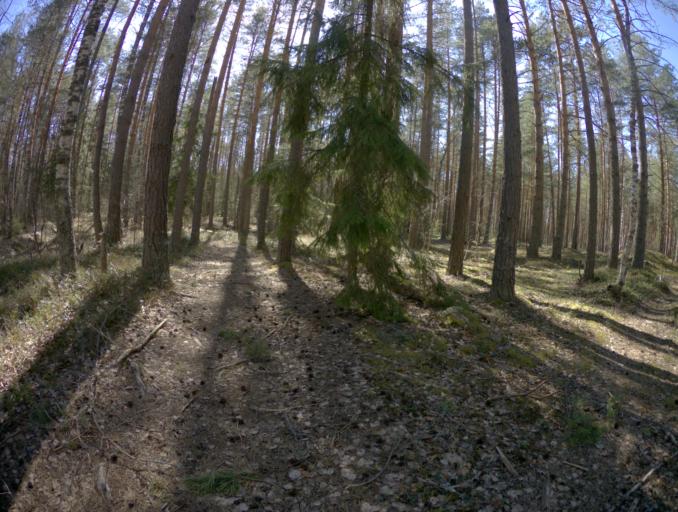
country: RU
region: Vladimir
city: Ivanishchi
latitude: 55.8211
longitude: 40.4182
